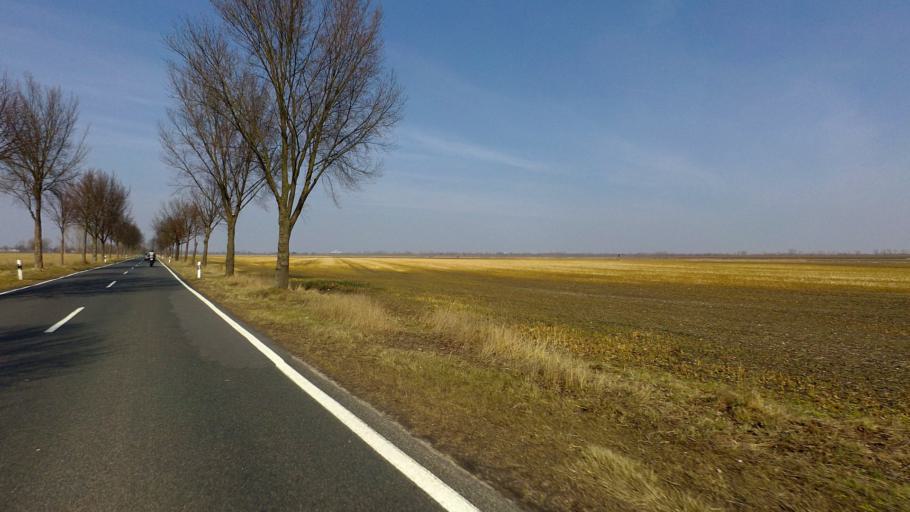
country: DE
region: Brandenburg
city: Ketzin
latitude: 52.4419
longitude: 12.8555
